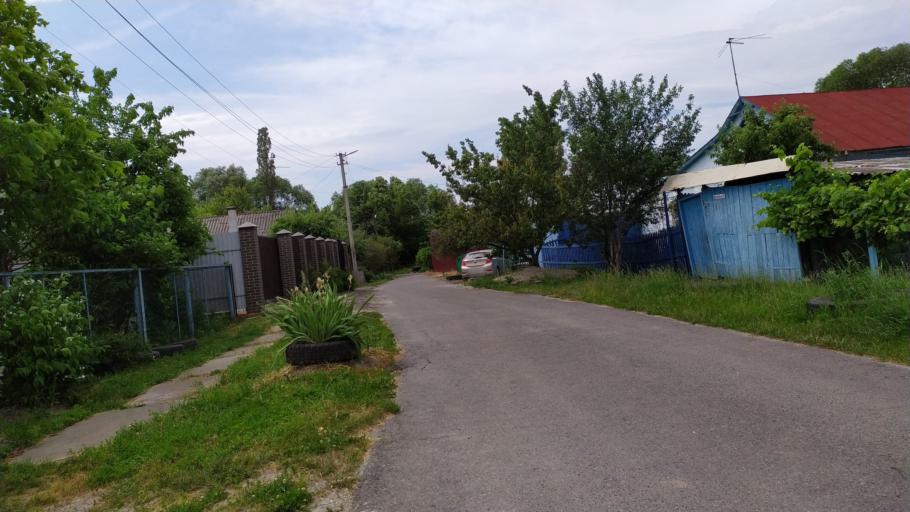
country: RU
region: Kursk
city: Kursk
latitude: 51.6622
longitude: 36.1535
